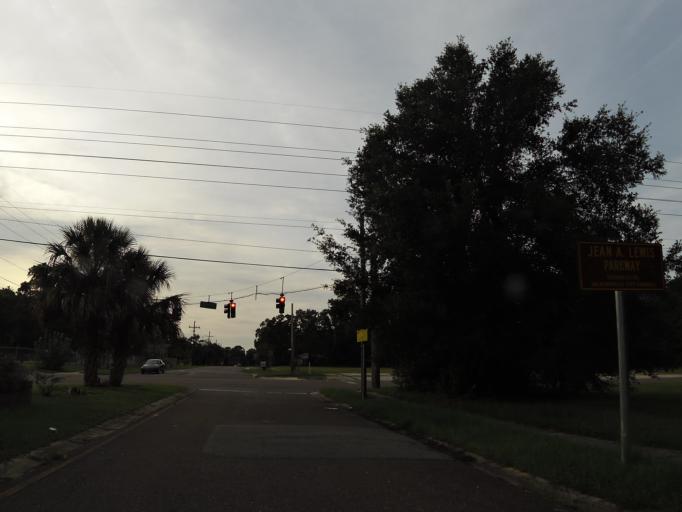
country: US
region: Florida
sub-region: Duval County
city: Jacksonville
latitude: 30.4036
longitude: -81.7200
